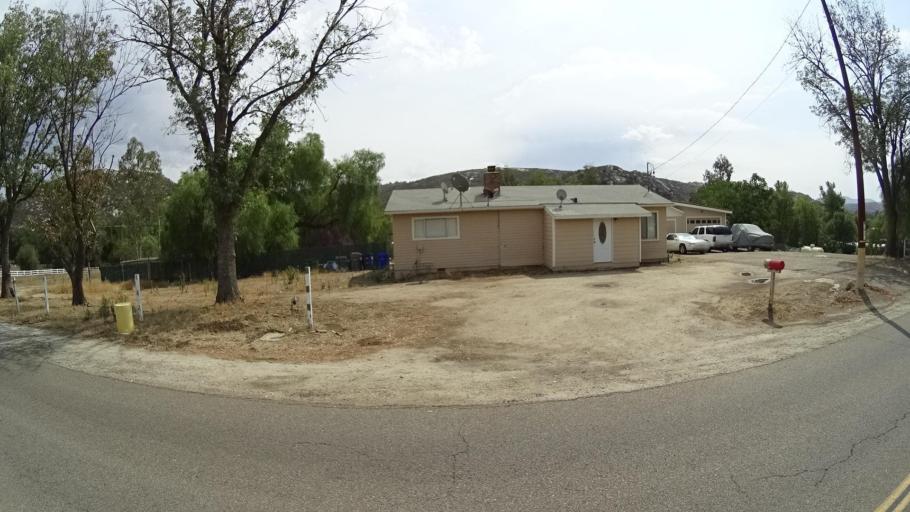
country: US
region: California
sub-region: San Diego County
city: Ramona
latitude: 33.0796
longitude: -116.8402
